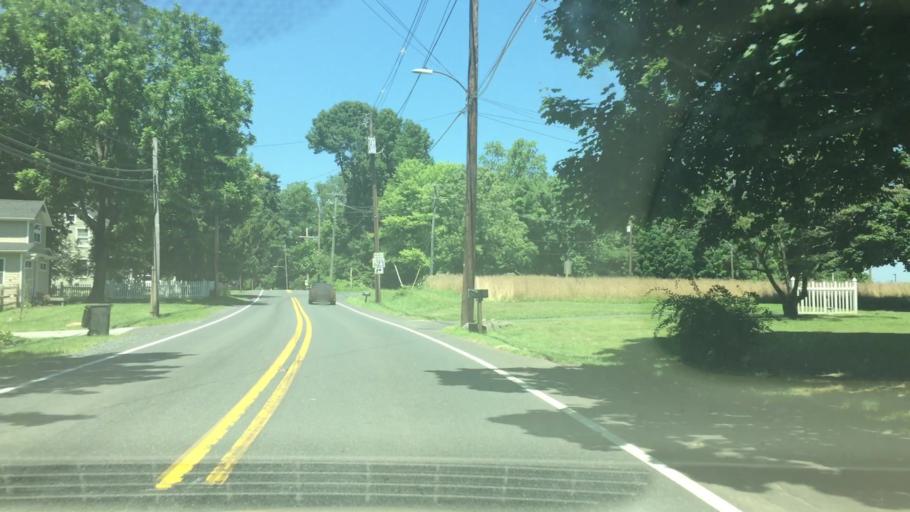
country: US
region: Maryland
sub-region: Harford County
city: Aberdeen
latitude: 39.6450
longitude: -76.2035
